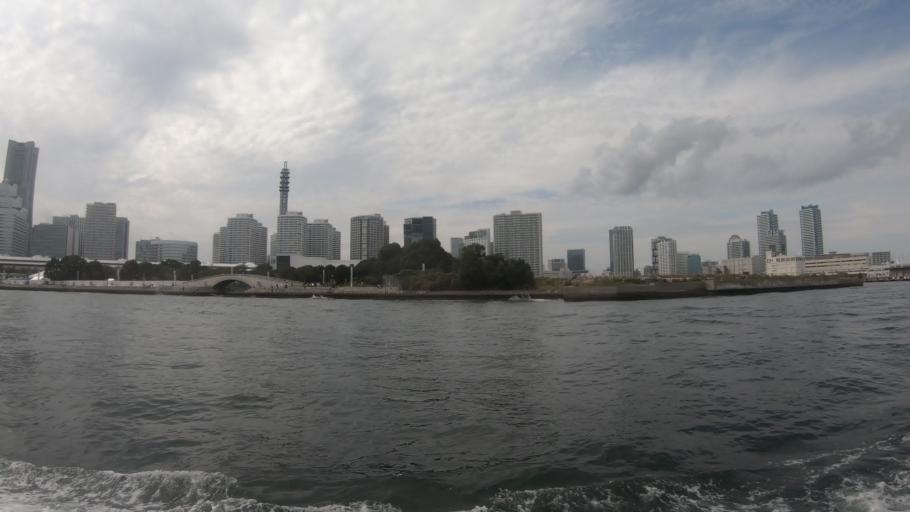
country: JP
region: Kanagawa
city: Yokohama
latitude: 35.4627
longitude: 139.6396
